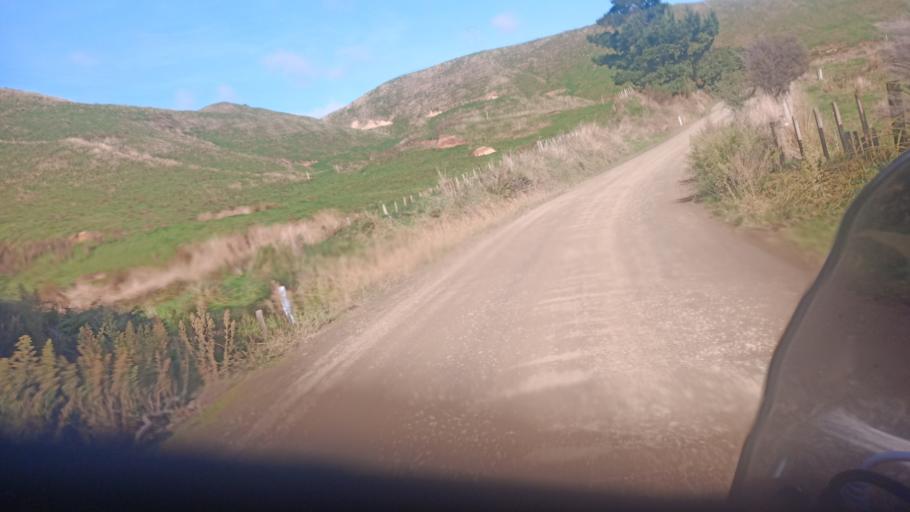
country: NZ
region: Bay of Plenty
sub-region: Opotiki District
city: Opotiki
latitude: -38.4382
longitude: 177.5434
